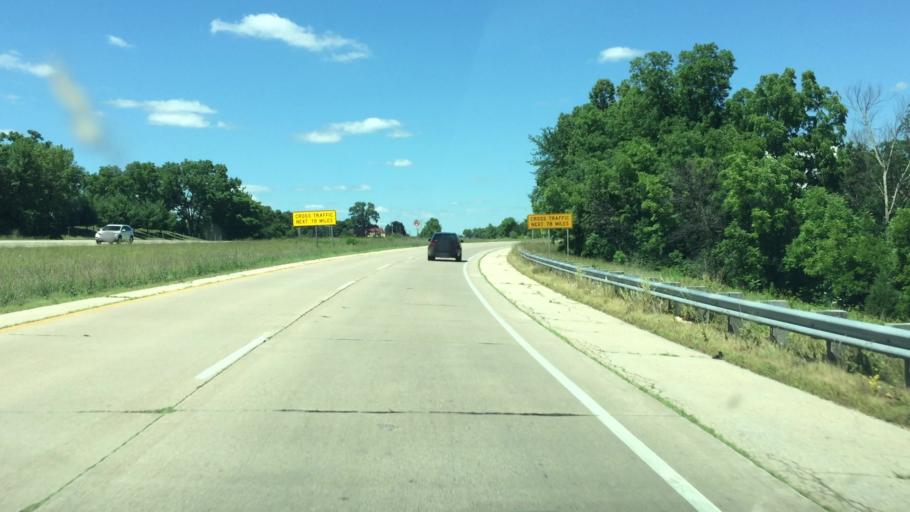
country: US
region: Illinois
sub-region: Jo Daviess County
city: East Dubuque
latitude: 42.5501
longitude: -90.6095
